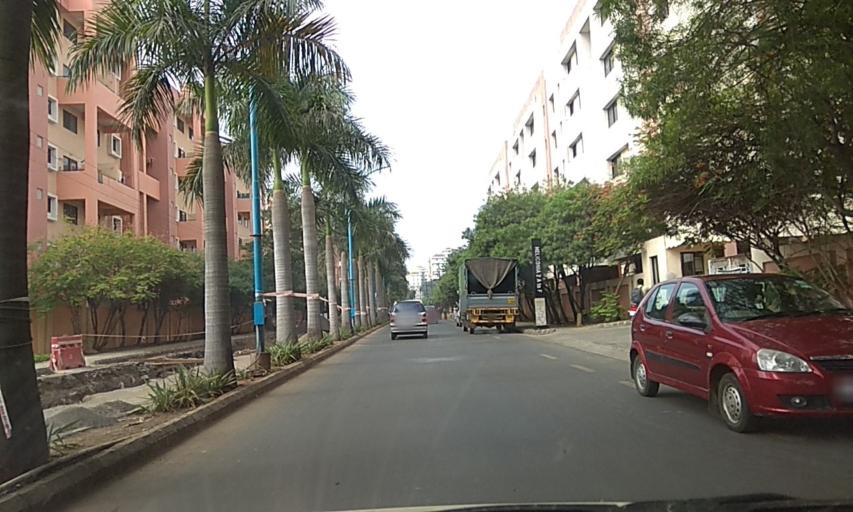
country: IN
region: Maharashtra
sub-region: Pune Division
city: Pune
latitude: 18.5086
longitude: 73.9291
